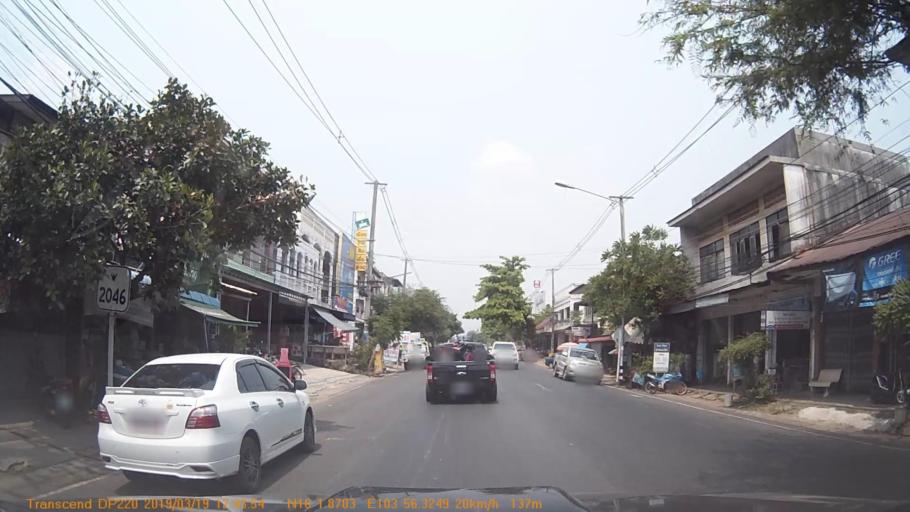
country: TH
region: Roi Et
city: Selaphum
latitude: 16.0311
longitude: 103.9388
